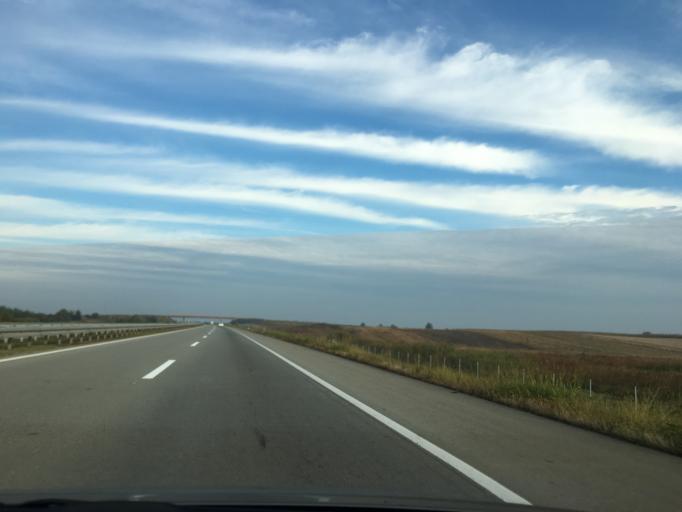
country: RS
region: Autonomna Pokrajina Vojvodina
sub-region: Juznobacki Okrug
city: Kovilj
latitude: 45.2251
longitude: 20.0566
